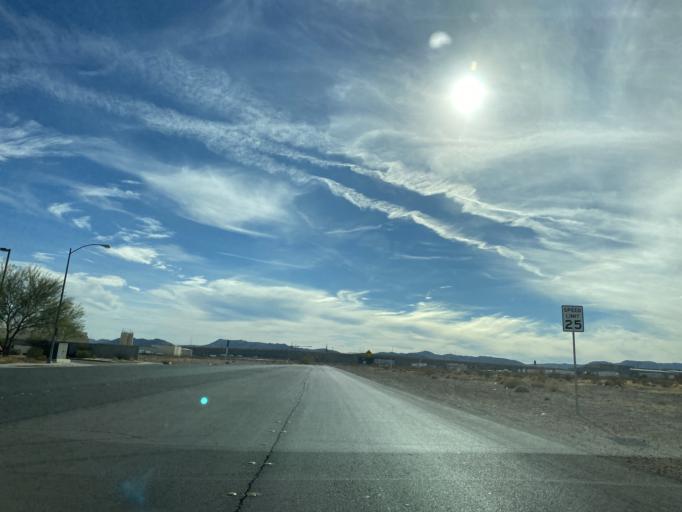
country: US
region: Nevada
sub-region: Clark County
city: Enterprise
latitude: 36.0312
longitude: -115.2257
